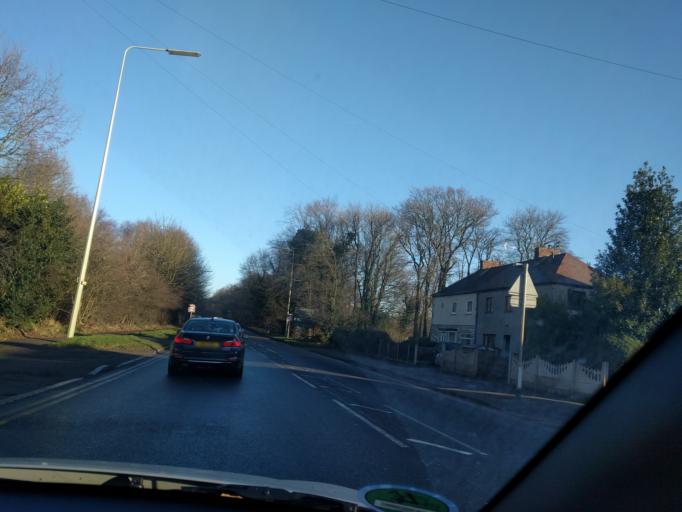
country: GB
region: England
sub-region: Staffordshire
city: Featherstone
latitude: 52.6479
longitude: -2.0830
